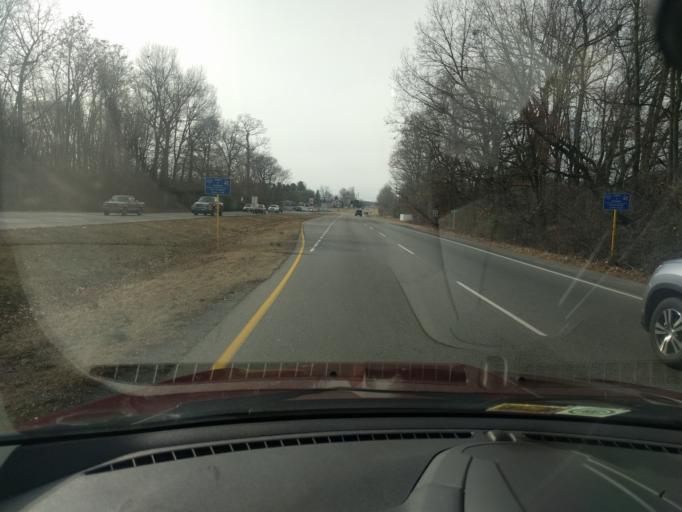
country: US
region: Virginia
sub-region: Augusta County
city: Lyndhurst
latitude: 38.0583
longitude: -78.9474
